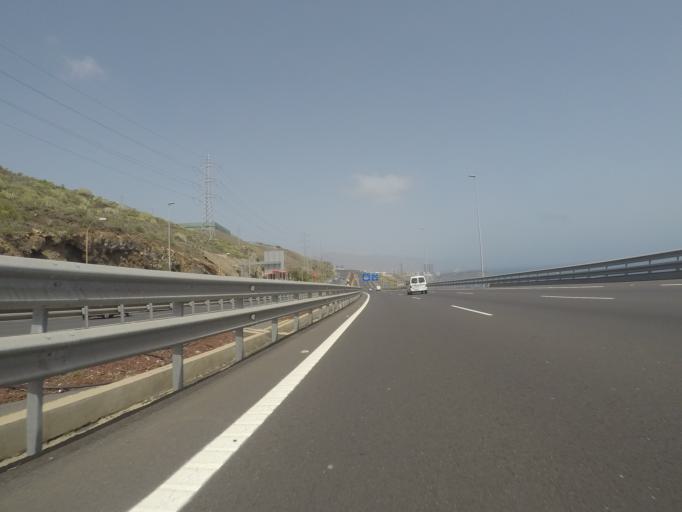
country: ES
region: Canary Islands
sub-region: Provincia de Santa Cruz de Tenerife
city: Santa Cruz de Tenerife
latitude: 28.4347
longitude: -16.2833
